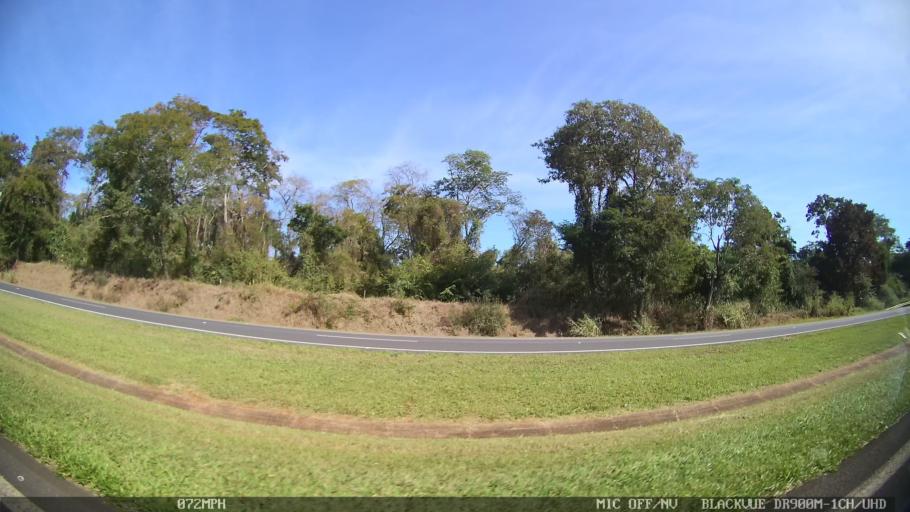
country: BR
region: Sao Paulo
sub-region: Pirassununga
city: Pirassununga
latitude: -21.9456
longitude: -47.4636
